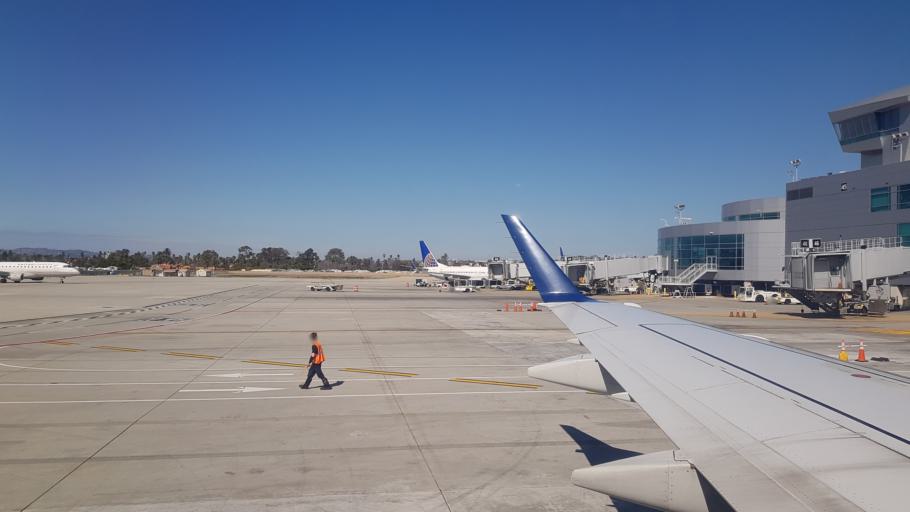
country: US
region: California
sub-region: San Diego County
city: San Diego
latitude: 32.7334
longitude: -117.2054
